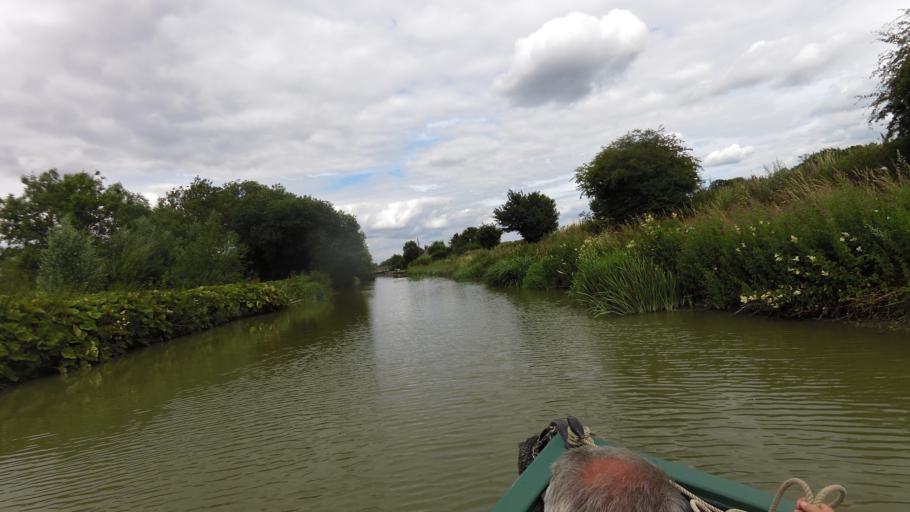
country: GB
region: England
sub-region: Wiltshire
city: Great Bedwyn
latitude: 51.3637
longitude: -1.6172
